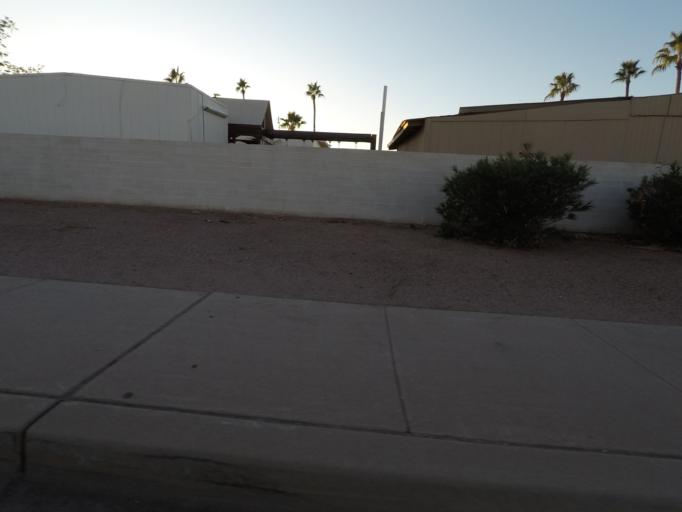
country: US
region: Arizona
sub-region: Maricopa County
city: Guadalupe
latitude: 33.3844
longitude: -111.9438
